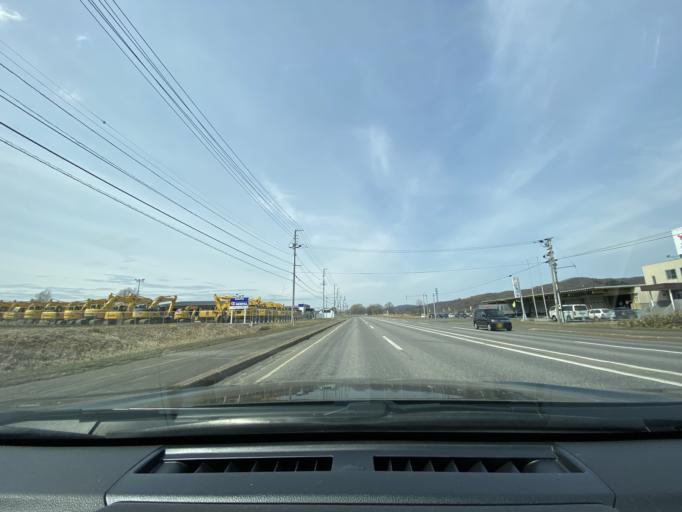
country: JP
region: Hokkaido
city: Kitami
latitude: 43.8019
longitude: 143.7916
